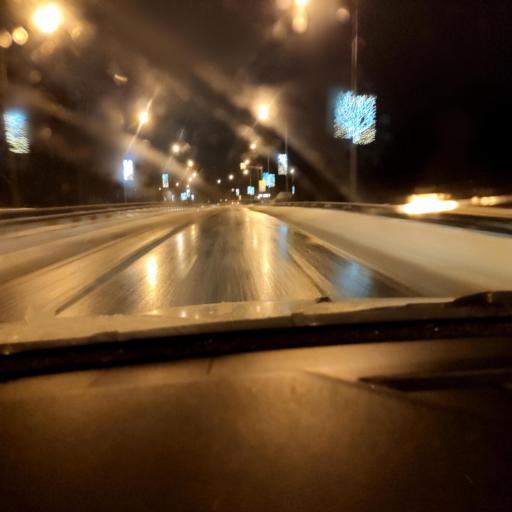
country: RU
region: Samara
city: Volzhskiy
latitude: 53.3628
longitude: 50.2027
